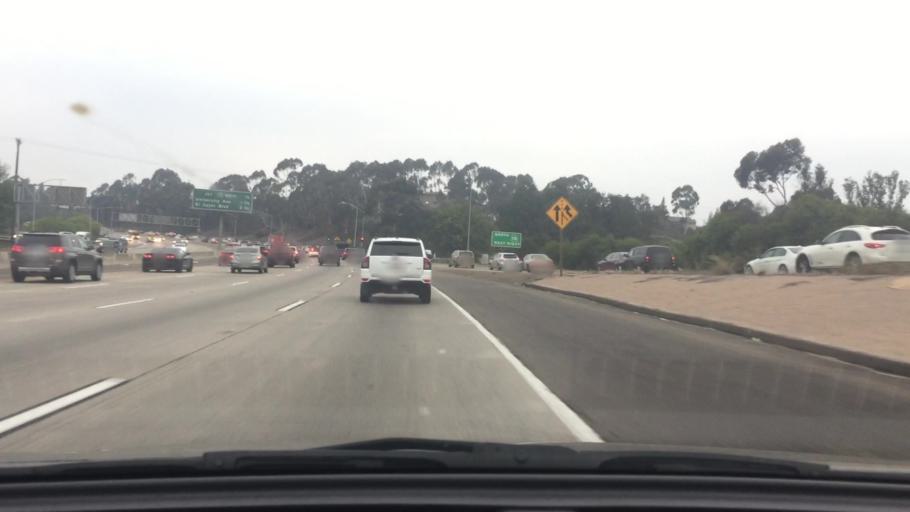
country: US
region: California
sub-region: San Diego County
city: National City
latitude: 32.7244
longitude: -117.1026
